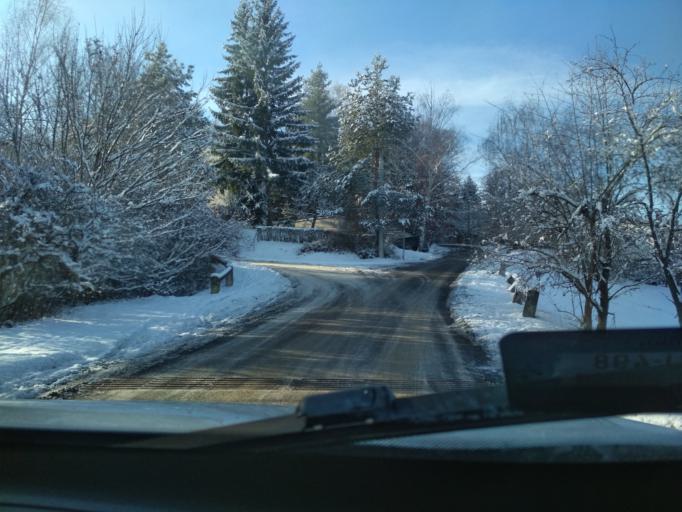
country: HU
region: Nograd
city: Somoskoujfalu
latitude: 48.1318
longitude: 19.8221
